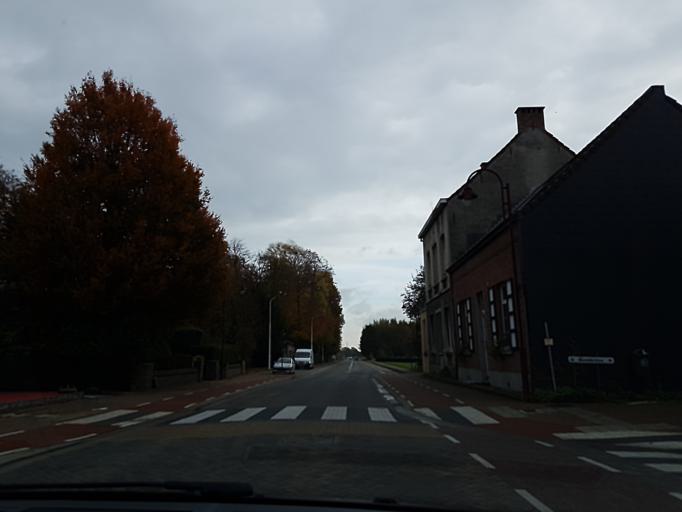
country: BE
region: Flanders
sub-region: Provincie Antwerpen
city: Boechout
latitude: 51.1593
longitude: 4.4970
